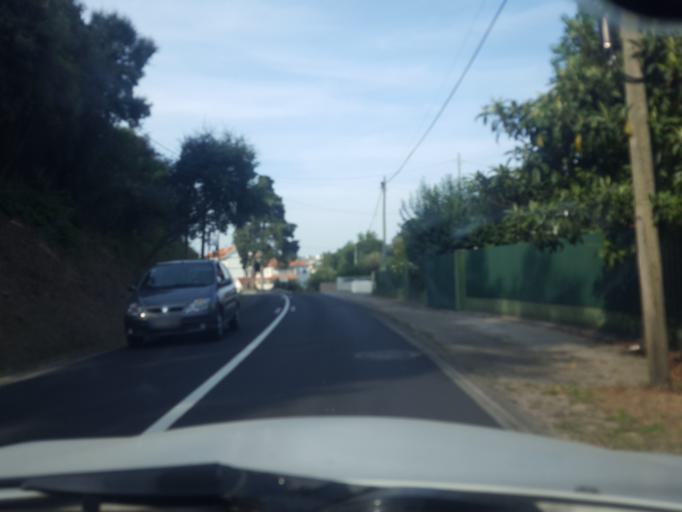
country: PT
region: Leiria
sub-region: Leiria
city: Leiria
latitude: 39.7118
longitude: -8.7895
